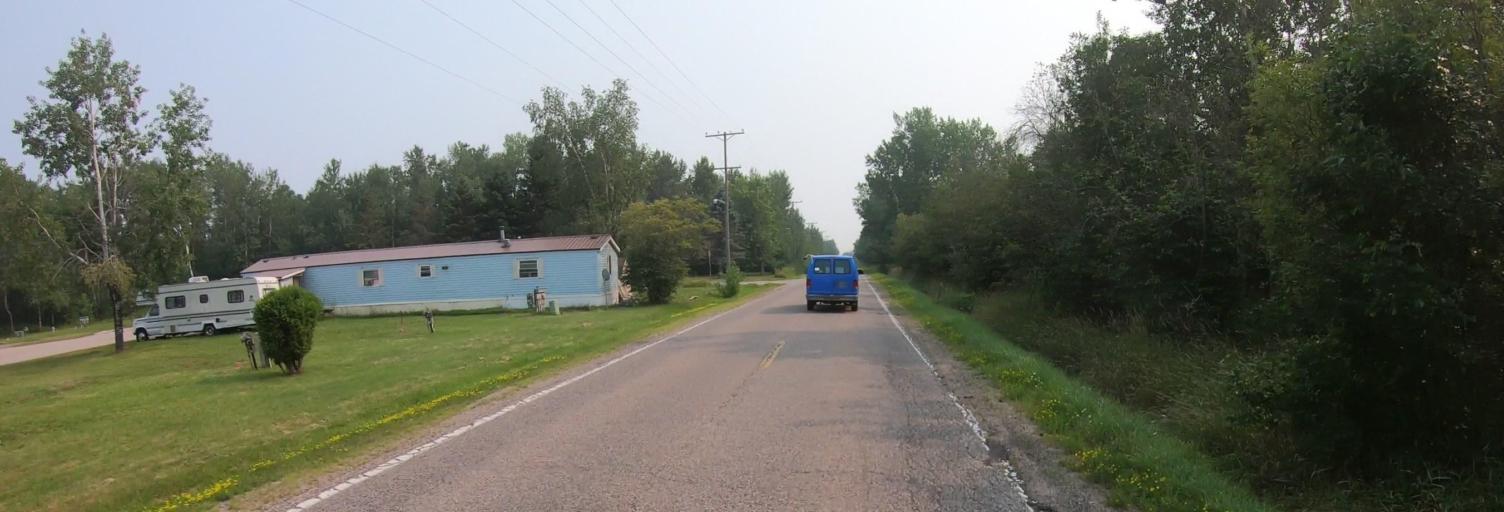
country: US
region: Michigan
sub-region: Chippewa County
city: Sault Ste. Marie
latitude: 46.4680
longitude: -84.3013
